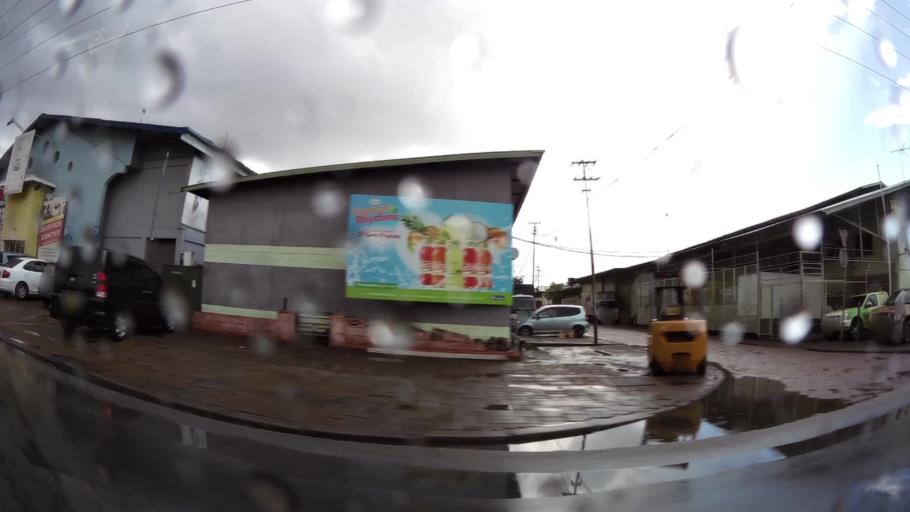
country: SR
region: Paramaribo
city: Paramaribo
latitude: 5.8190
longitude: -55.1746
